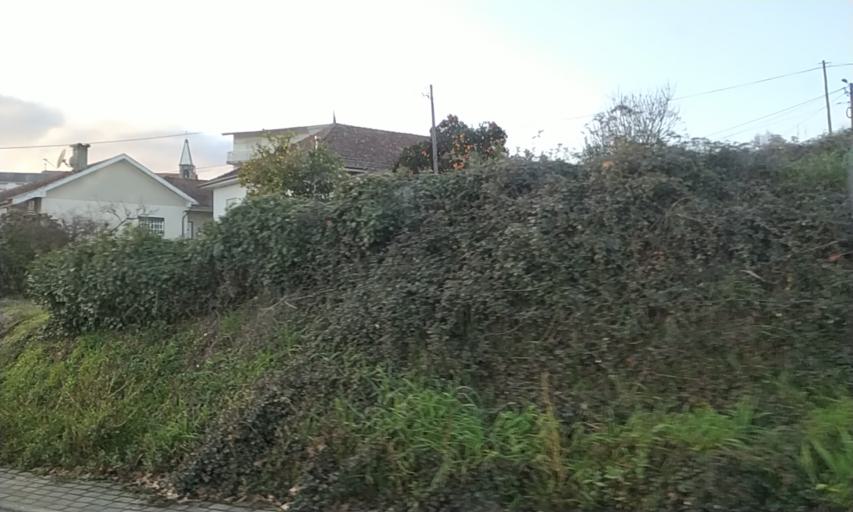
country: PT
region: Vila Real
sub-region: Mondim de Basto
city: Mondim de Basto
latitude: 41.4438
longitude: -7.9655
